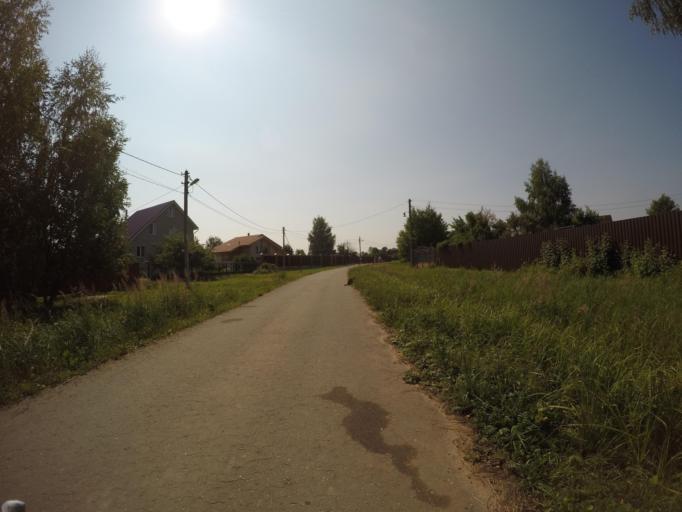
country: RU
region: Moskovskaya
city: Rechitsy
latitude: 55.6407
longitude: 38.5090
